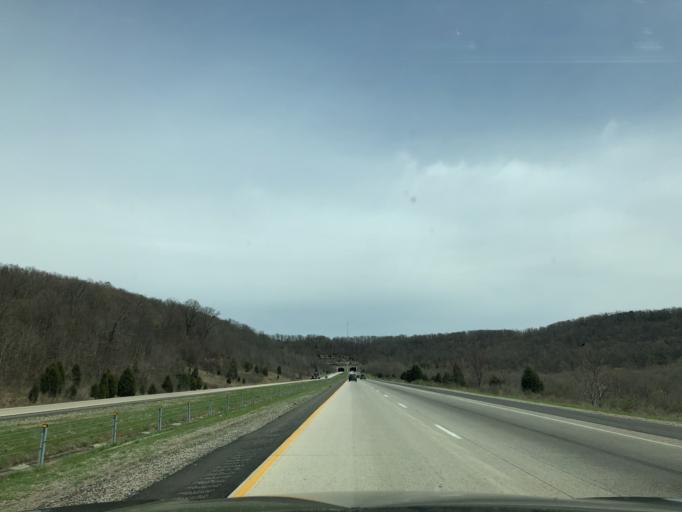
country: US
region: Arkansas
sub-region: Washington County
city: West Fork
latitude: 35.7568
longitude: -94.1962
